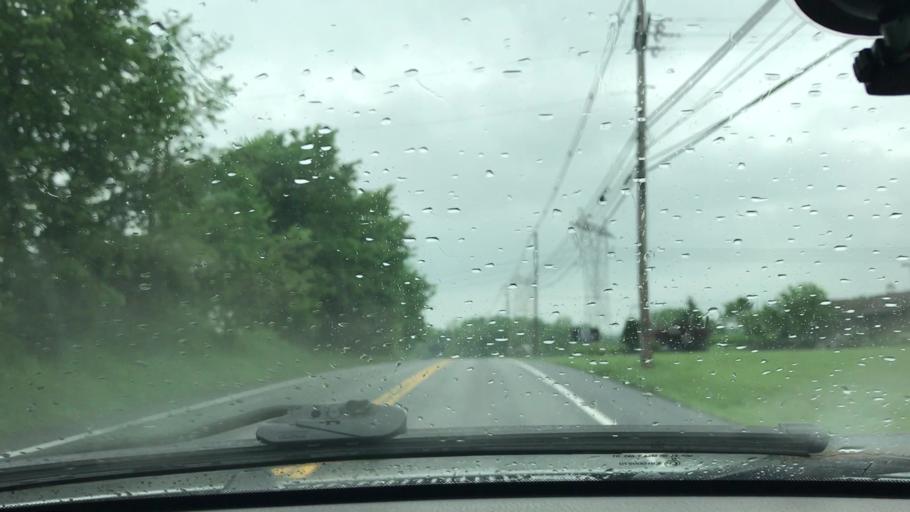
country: US
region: Pennsylvania
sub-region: Lancaster County
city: Elizabethtown
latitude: 40.1750
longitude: -76.6578
